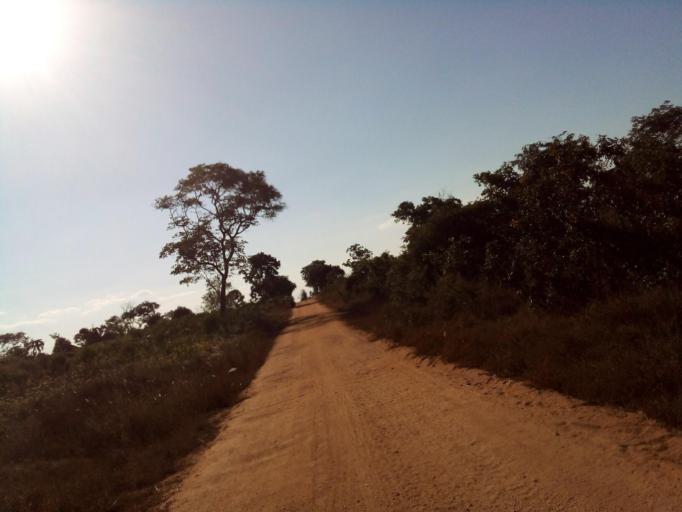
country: MZ
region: Zambezia
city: Quelimane
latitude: -17.5019
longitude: 36.5805
